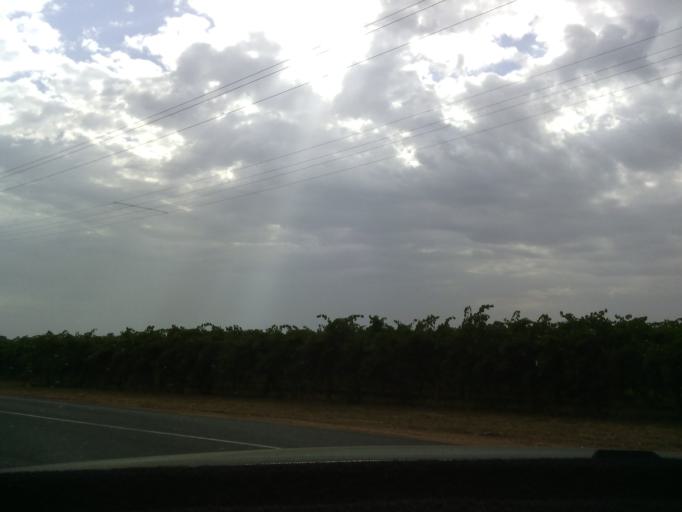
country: AU
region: South Australia
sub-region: Berri and Barmera
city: Monash
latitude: -34.2640
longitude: 140.5751
